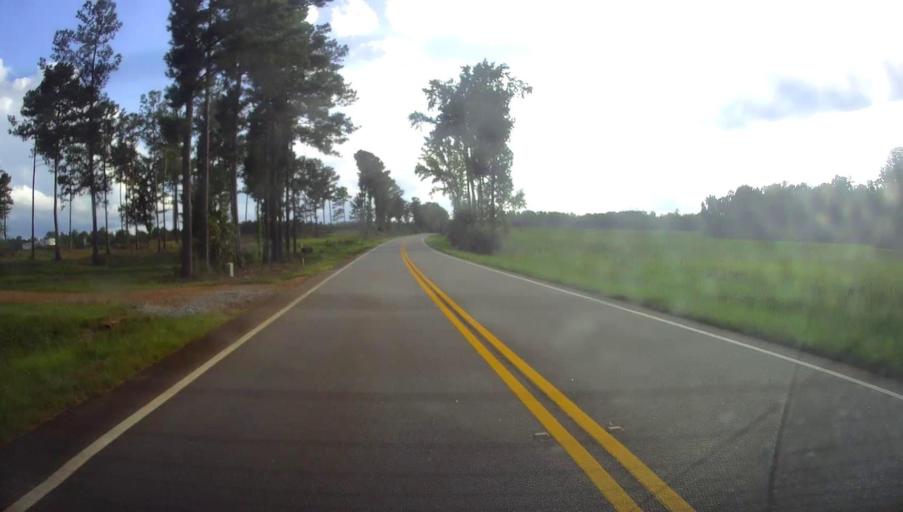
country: US
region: Georgia
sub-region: Monroe County
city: Forsyth
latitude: 32.9087
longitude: -83.9782
